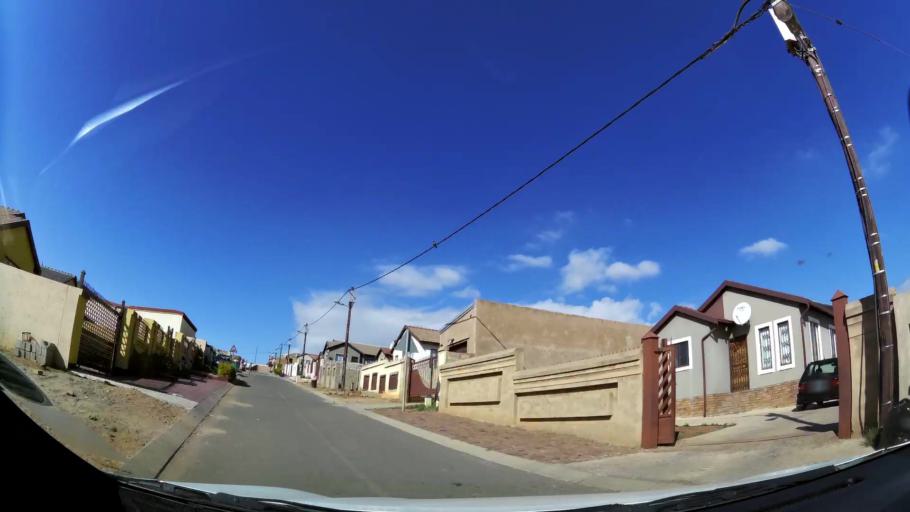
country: ZA
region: Gauteng
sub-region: City of Tshwane Metropolitan Municipality
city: Cullinan
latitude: -25.6916
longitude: 28.4143
